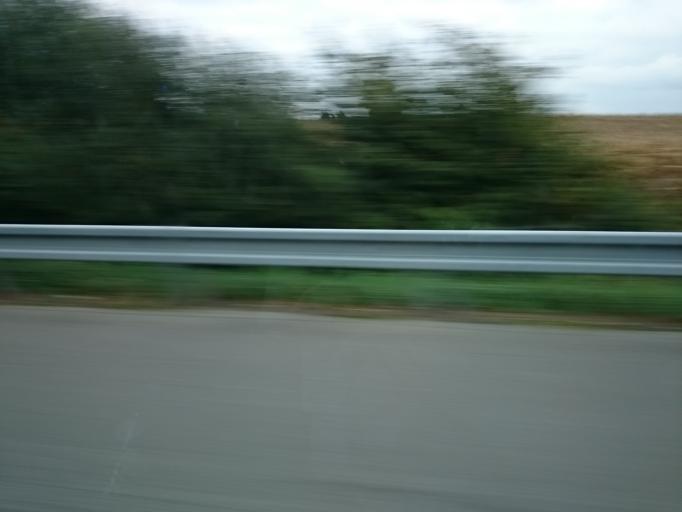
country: FR
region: Brittany
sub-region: Departement du Morbihan
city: Landevant
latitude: 47.7640
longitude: -3.1451
